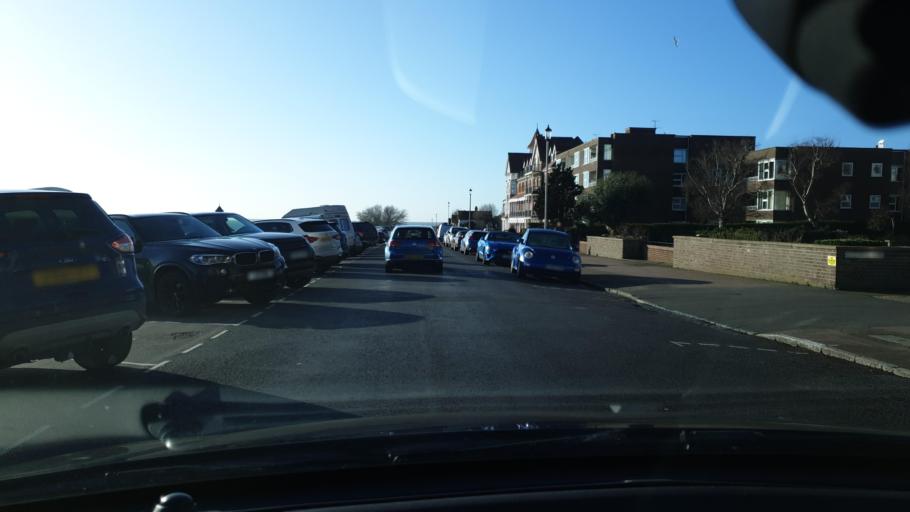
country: GB
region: England
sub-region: Essex
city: Frinton-on-Sea
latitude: 51.8282
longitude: 1.2454
